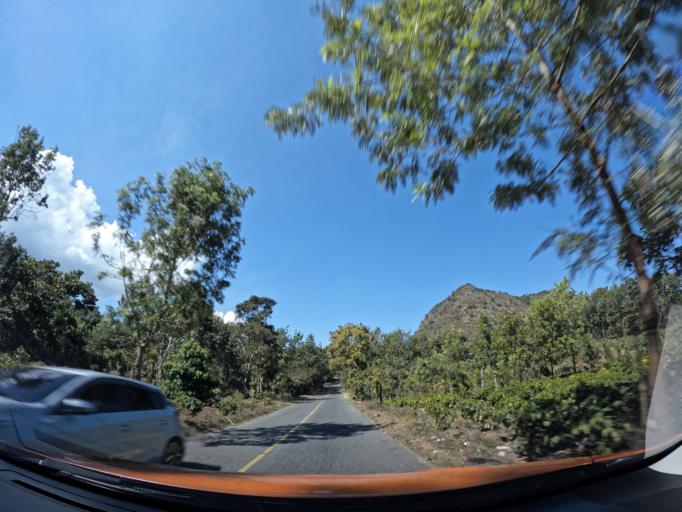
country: GT
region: Solola
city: Santiago Atitlan
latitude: 14.6595
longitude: -91.1710
